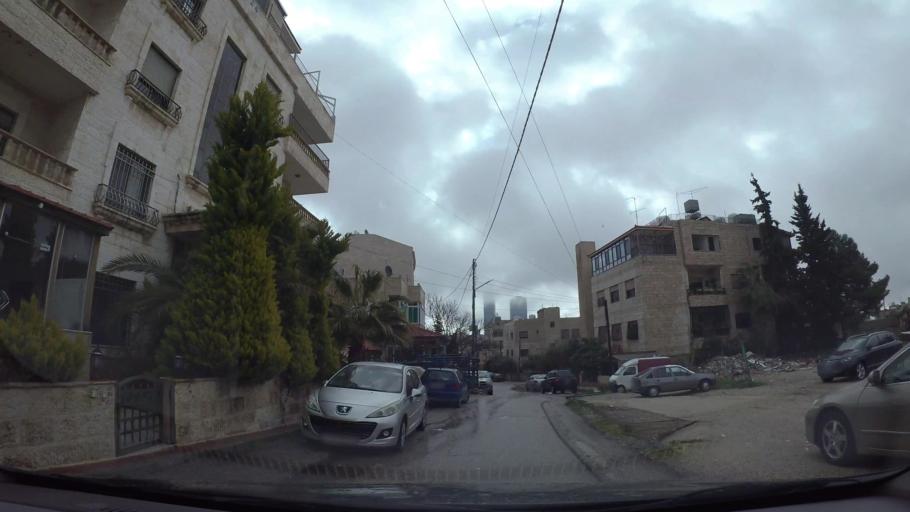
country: JO
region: Amman
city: Wadi as Sir
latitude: 31.9691
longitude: 35.8567
